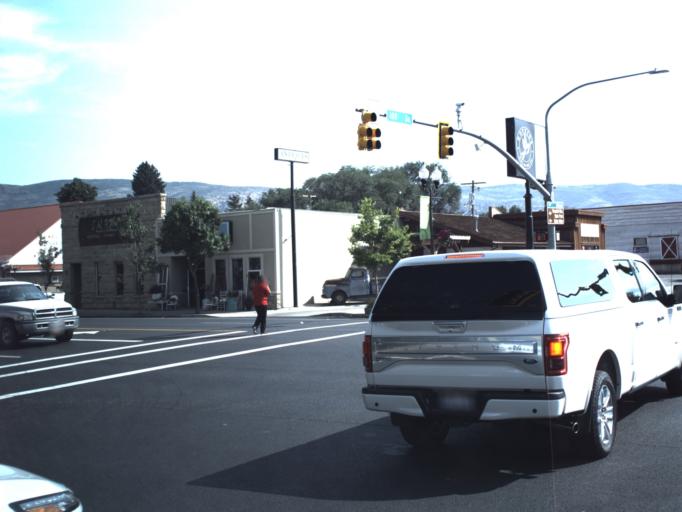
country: US
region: Utah
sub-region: Wasatch County
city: Heber
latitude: 40.5063
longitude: -111.4137
